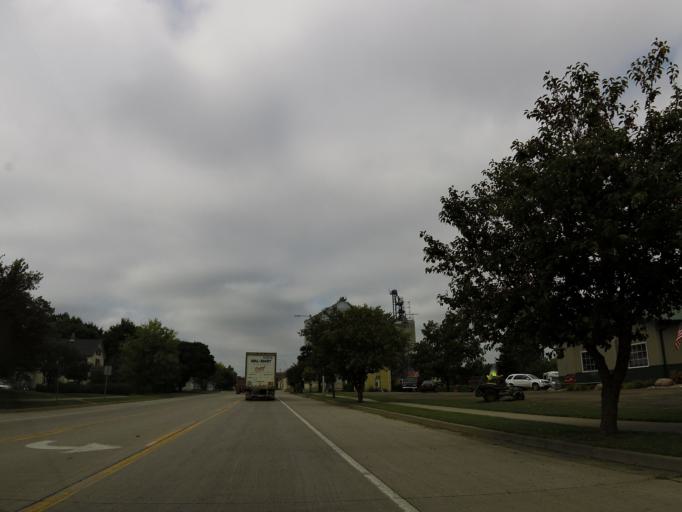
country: US
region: Minnesota
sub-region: Renville County
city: Olivia
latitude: 44.7765
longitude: -94.9843
